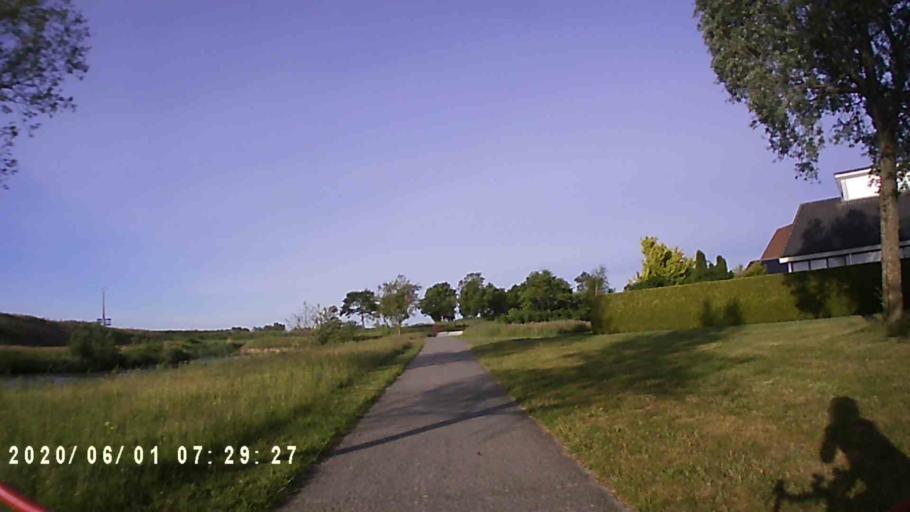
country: NL
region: Friesland
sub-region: Gemeente Dongeradeel
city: Dokkum
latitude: 53.3128
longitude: 6.0115
